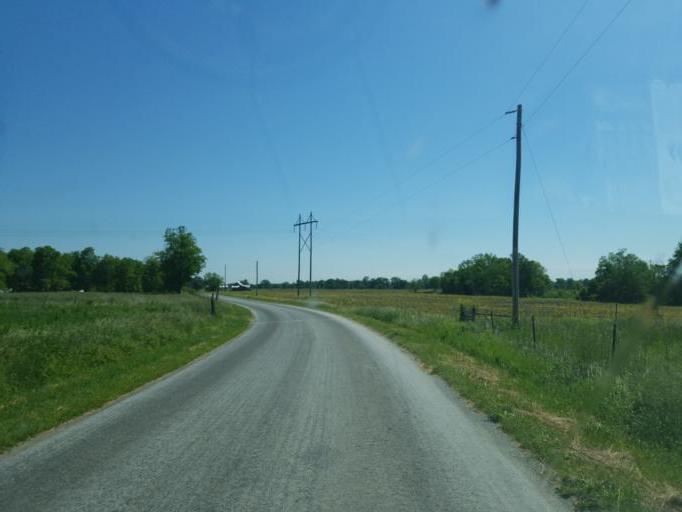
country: US
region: Ohio
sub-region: Hardin County
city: Kenton
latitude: 40.6034
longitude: -83.5173
